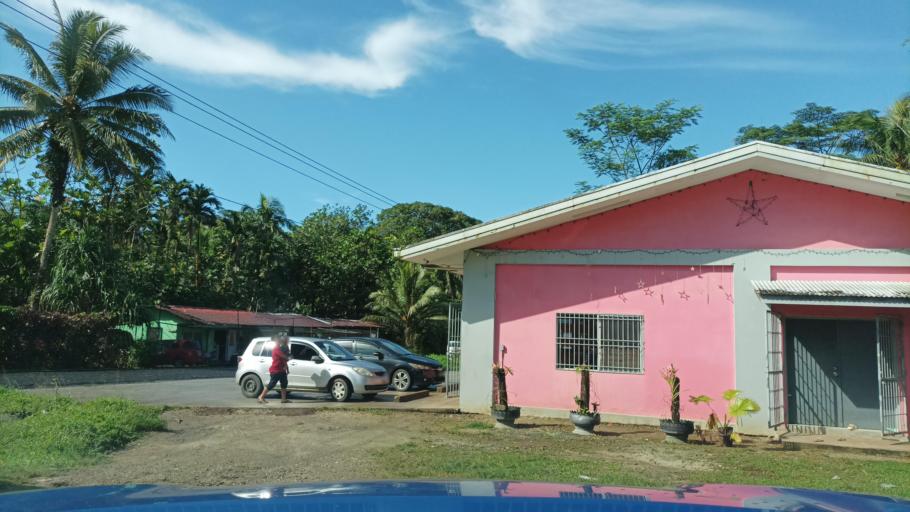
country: FM
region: Pohnpei
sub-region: Sokehs Municipality
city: Palikir - National Government Center
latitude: 6.9232
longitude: 158.1674
